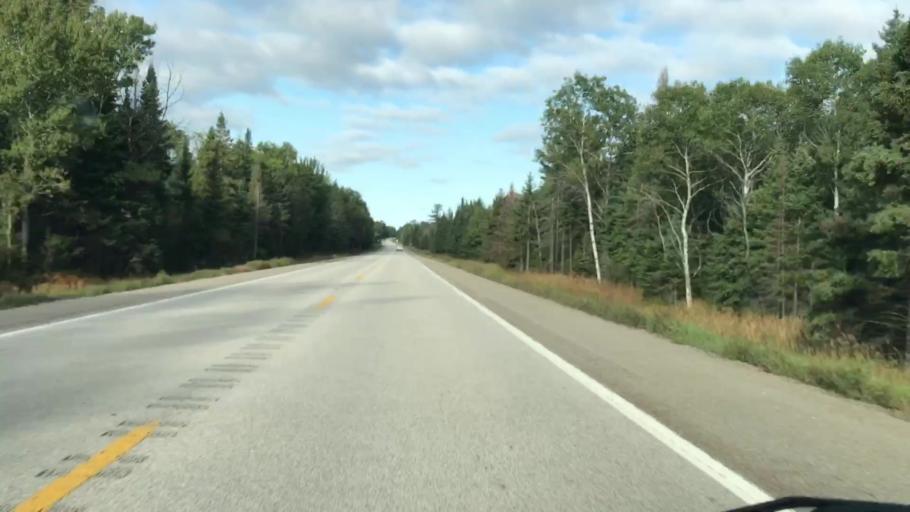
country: US
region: Michigan
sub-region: Luce County
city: Newberry
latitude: 46.3320
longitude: -85.0690
